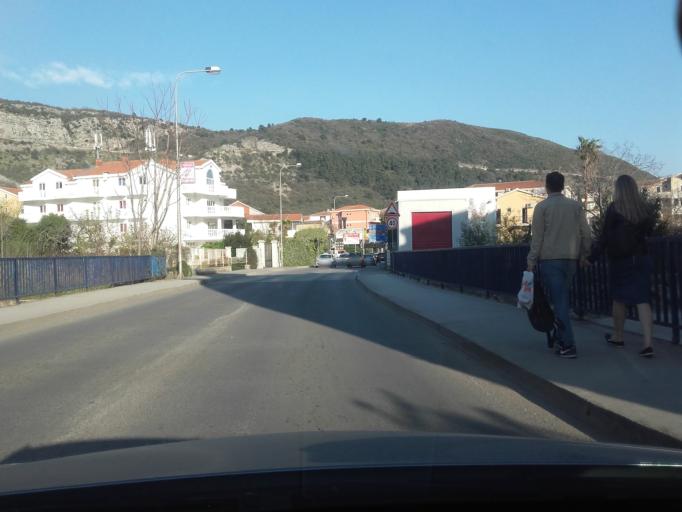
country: ME
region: Budva
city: Budva
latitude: 42.2946
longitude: 18.8423
